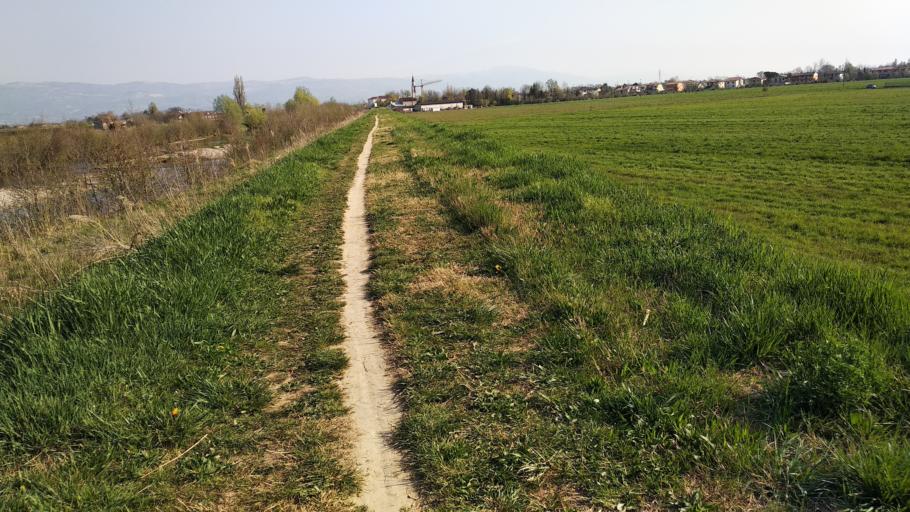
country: IT
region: Veneto
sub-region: Provincia di Vicenza
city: Dueville
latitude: 45.6053
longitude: 11.5408
